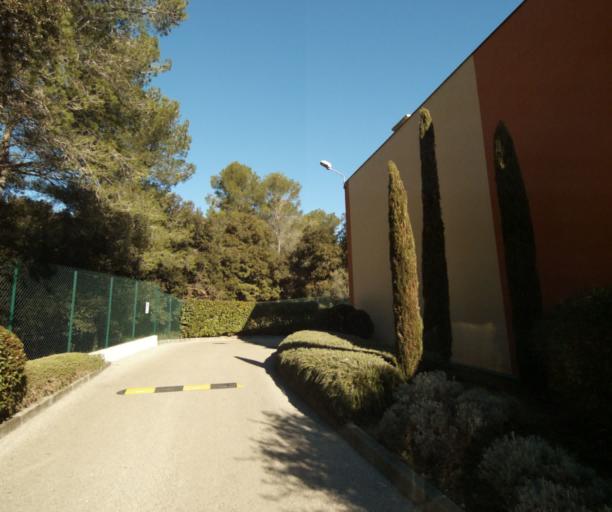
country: FR
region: Provence-Alpes-Cote d'Azur
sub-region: Departement des Alpes-Maritimes
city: Biot
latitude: 43.6094
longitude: 7.0700
